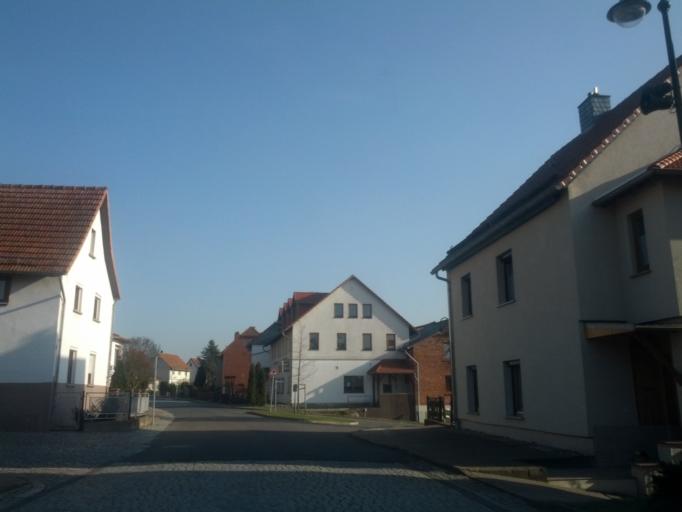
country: DE
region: Thuringia
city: Ifta
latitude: 51.0623
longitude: 10.1819
